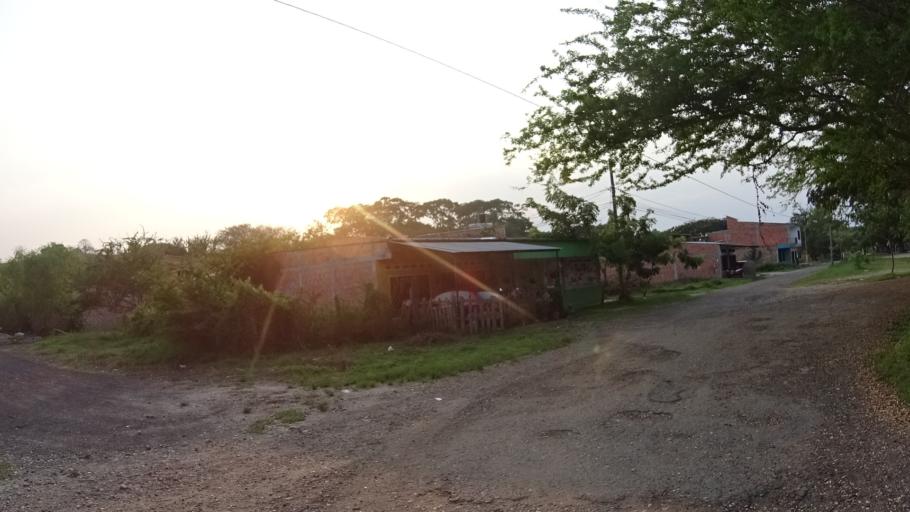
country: CO
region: Cundinamarca
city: Puerto Salgar
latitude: 5.4702
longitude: -74.6695
